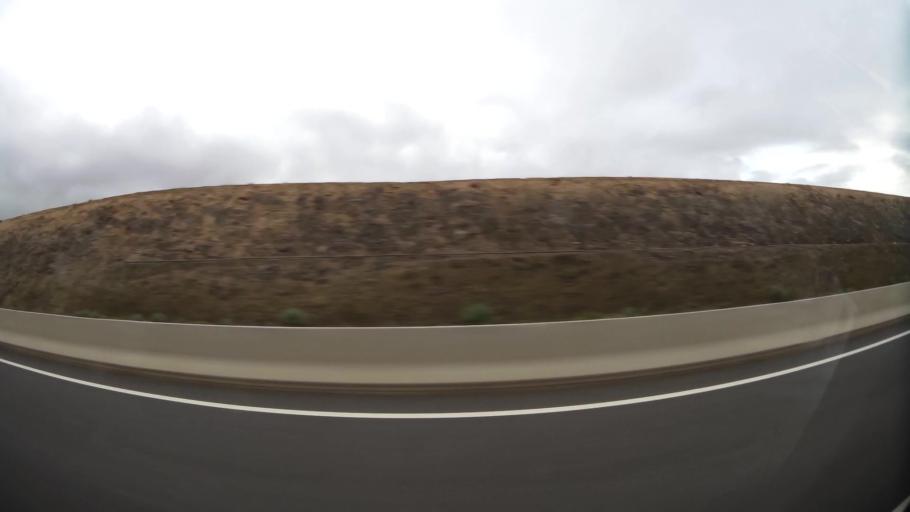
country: MA
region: Taza-Al Hoceima-Taounate
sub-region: Taza
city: Guercif
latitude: 34.3885
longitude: -3.2218
